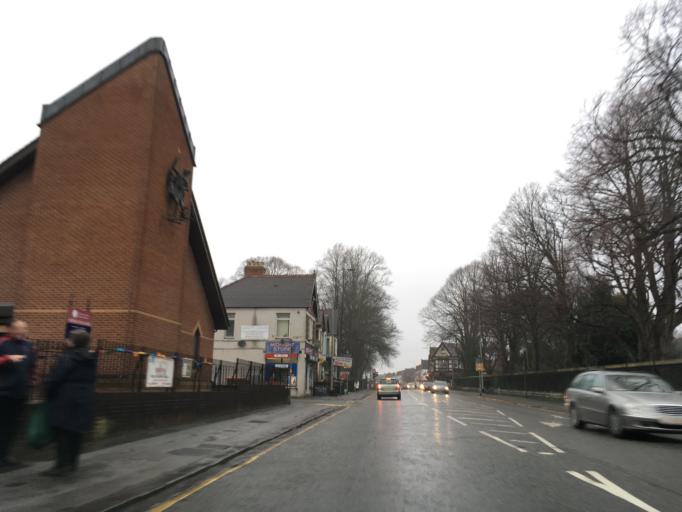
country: GB
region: Wales
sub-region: Cardiff
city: Cardiff
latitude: 51.4978
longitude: -3.1832
